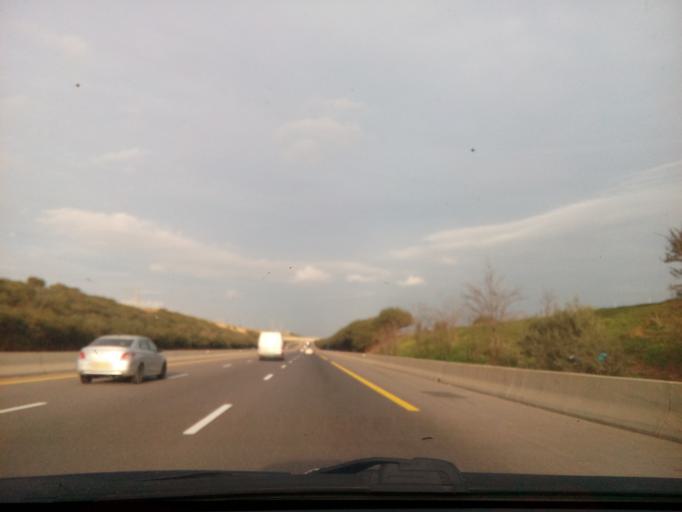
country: DZ
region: Relizane
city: Relizane
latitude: 35.7448
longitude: 0.3446
